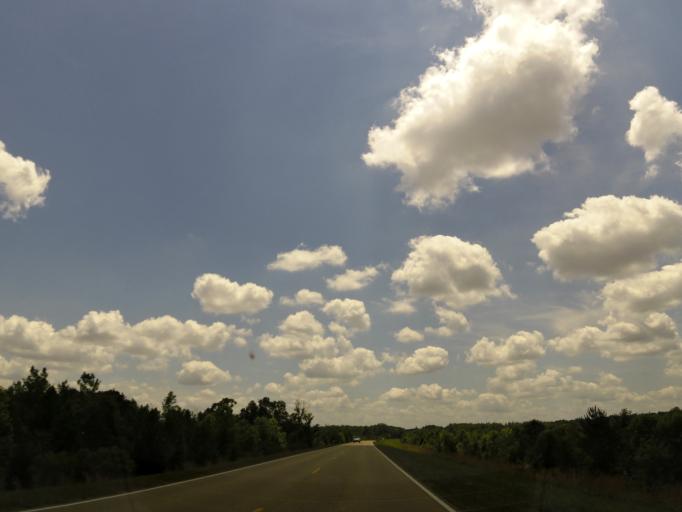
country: US
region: Mississippi
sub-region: Lee County
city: Tupelo
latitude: 34.3156
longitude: -88.7174
